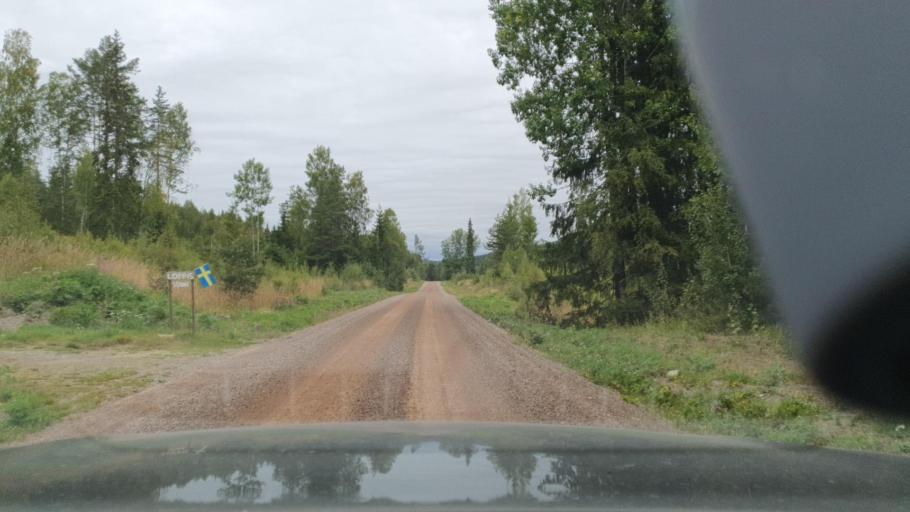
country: SE
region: Vaermland
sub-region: Eda Kommun
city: Charlottenberg
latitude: 60.0769
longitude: 12.5256
